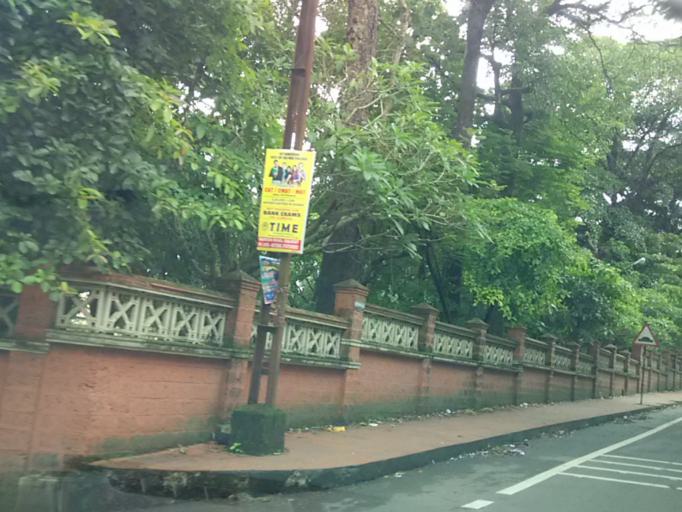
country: IN
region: Kerala
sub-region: Kozhikode
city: Mavoor
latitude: 11.3197
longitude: 75.9320
